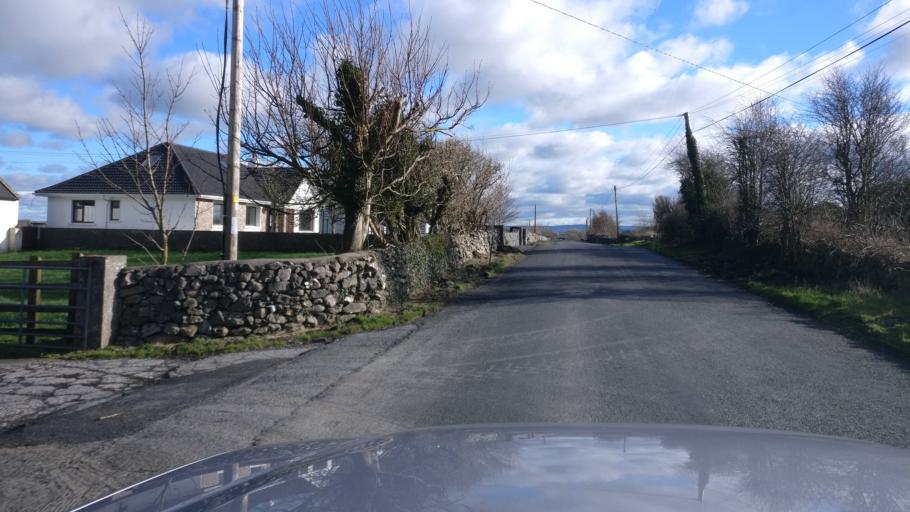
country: IE
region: Connaught
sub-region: County Galway
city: Oranmore
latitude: 53.2587
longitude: -8.8593
